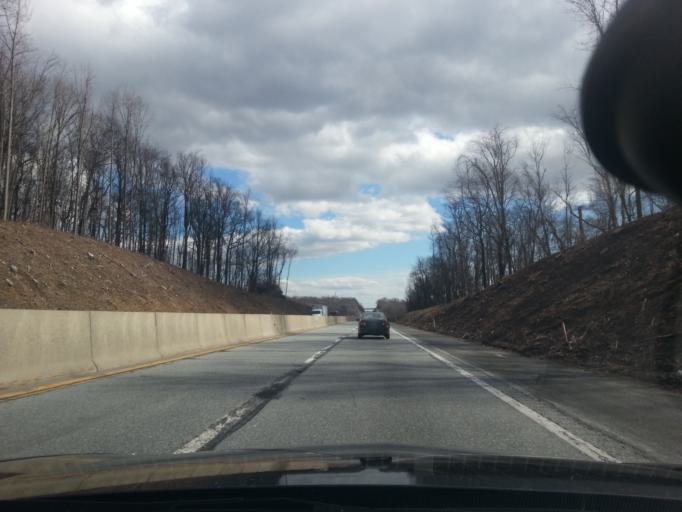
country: US
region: Pennsylvania
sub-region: Bucks County
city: Spinnerstown
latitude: 40.4746
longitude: -75.4565
